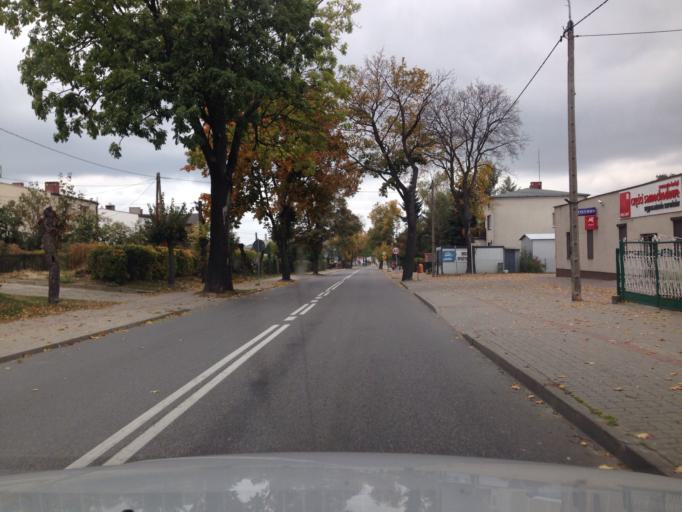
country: PL
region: Warmian-Masurian Voivodeship
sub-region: Powiat ilawski
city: Lubawa
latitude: 53.5002
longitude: 19.7552
